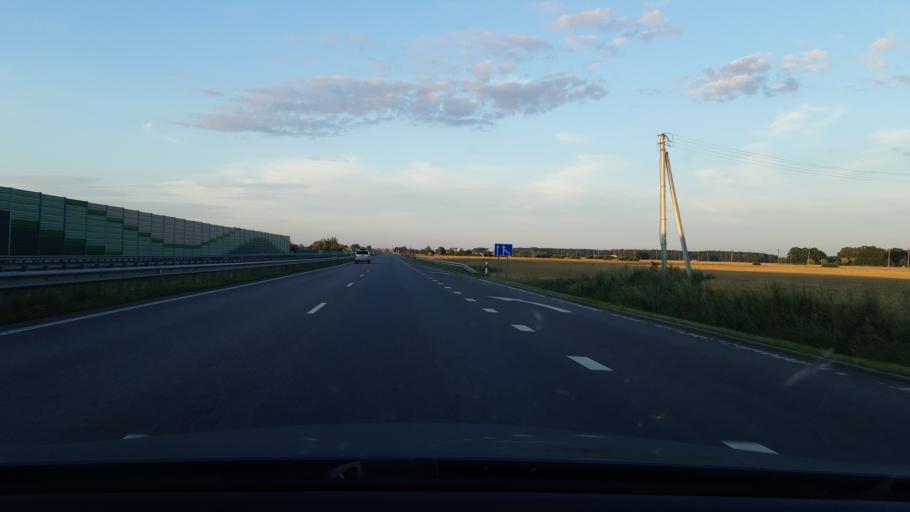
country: LT
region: Kauno apskritis
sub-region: Kauno rajonas
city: Mastaiciai
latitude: 54.7946
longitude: 23.8097
